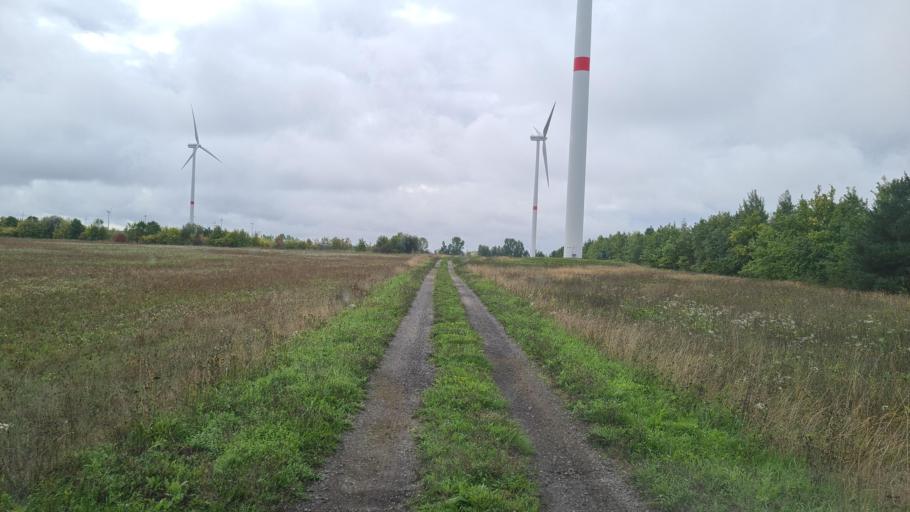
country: DE
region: Brandenburg
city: Sallgast
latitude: 51.5598
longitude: 13.8232
